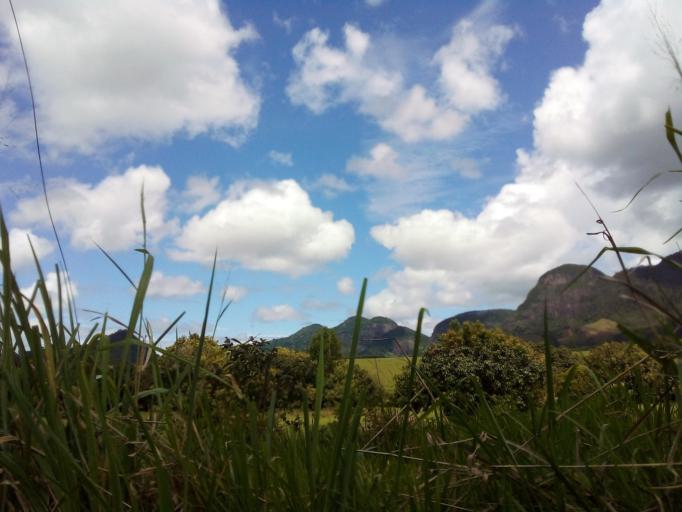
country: BR
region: Espirito Santo
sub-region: Ibiracu
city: Ibiracu
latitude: -19.8806
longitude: -40.3629
